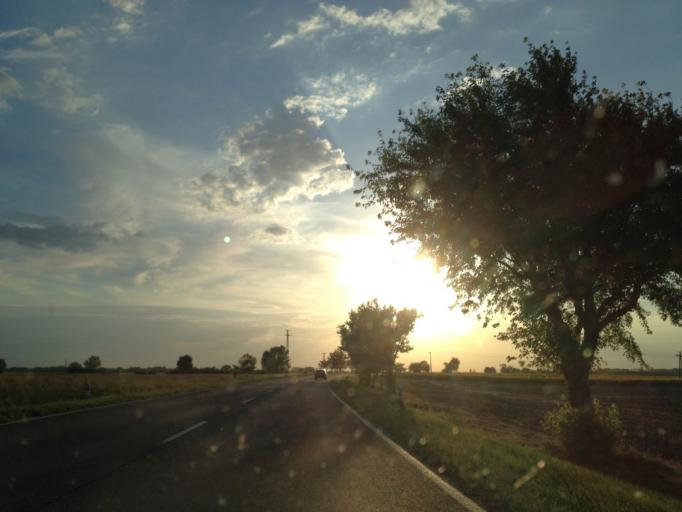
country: HU
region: Gyor-Moson-Sopron
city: Kimle
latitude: 47.8002
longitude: 17.3815
